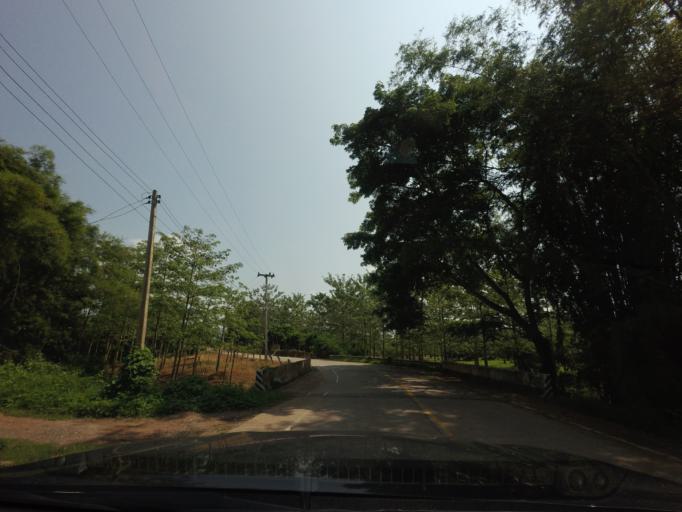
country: TH
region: Nan
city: Nan
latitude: 18.8585
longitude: 100.8071
